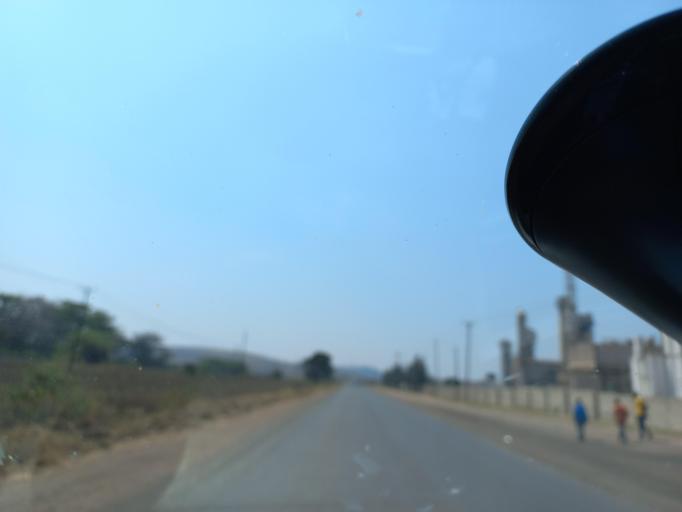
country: ZM
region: Lusaka
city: Kafue
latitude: -15.7546
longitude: 28.1682
